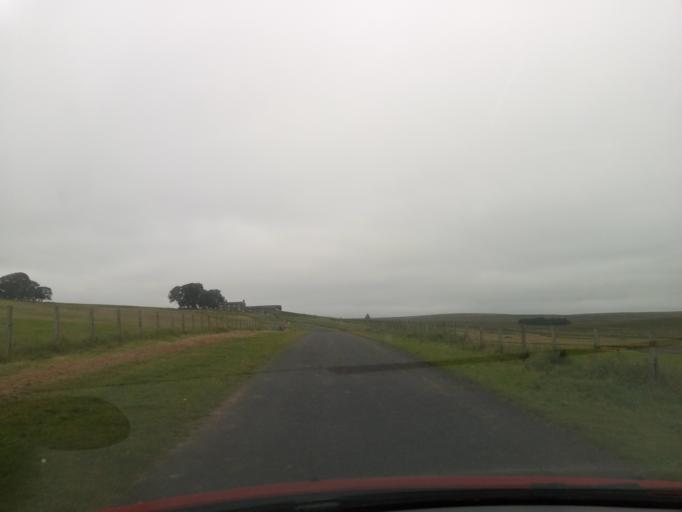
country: GB
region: England
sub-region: Northumberland
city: Rochester
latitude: 55.2920
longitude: -2.2069
